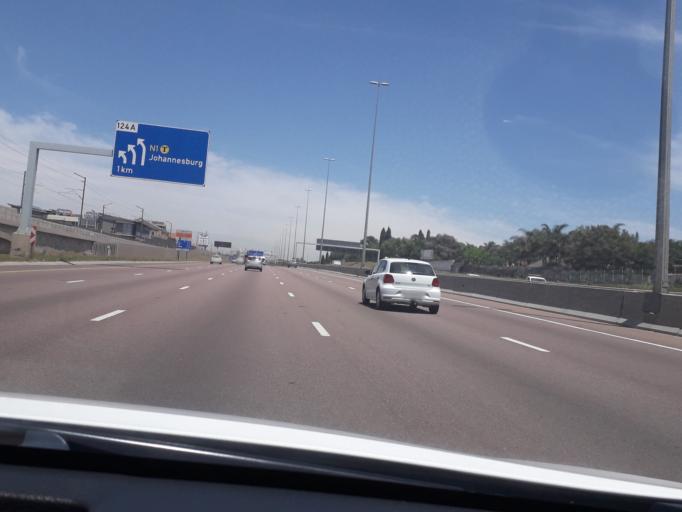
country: ZA
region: Gauteng
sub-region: City of Tshwane Metropolitan Municipality
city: Centurion
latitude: -25.8705
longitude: 28.1854
